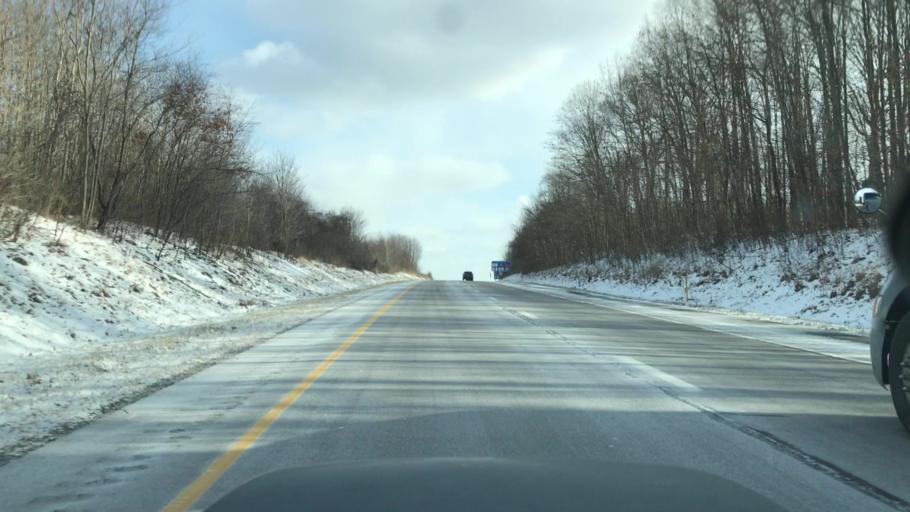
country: US
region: Pennsylvania
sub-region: Jefferson County
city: Brookville
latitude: 41.1760
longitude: -79.1174
